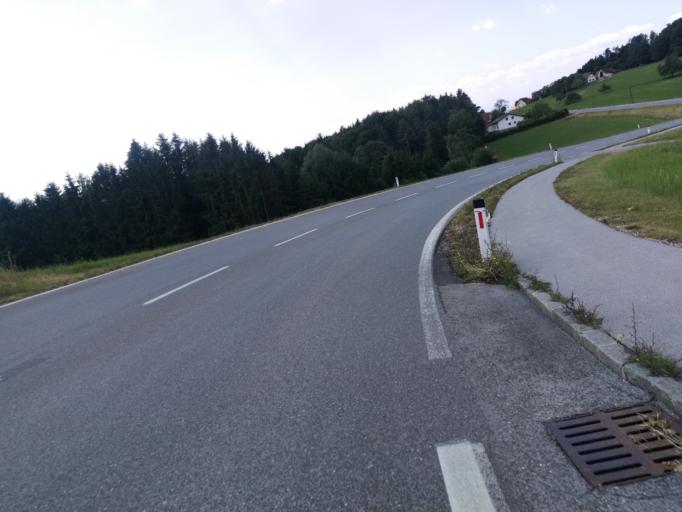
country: AT
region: Styria
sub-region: Politischer Bezirk Graz-Umgebung
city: Kumberg
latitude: 47.1314
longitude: 15.5146
